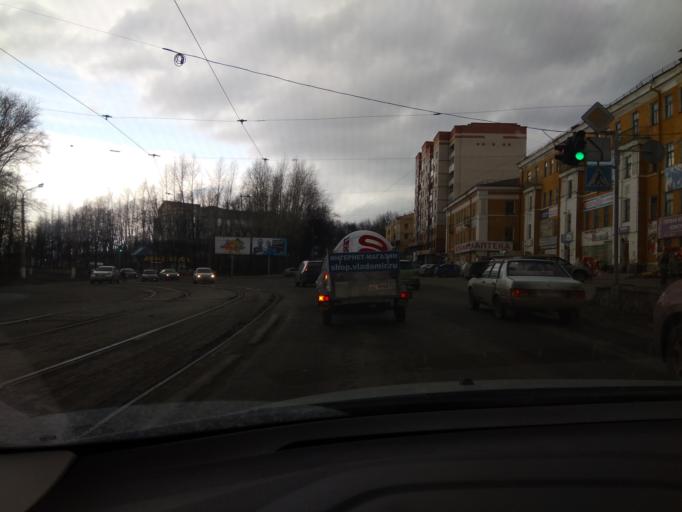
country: RU
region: Chelyabinsk
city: Zlatoust
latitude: 55.1035
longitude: 59.7192
